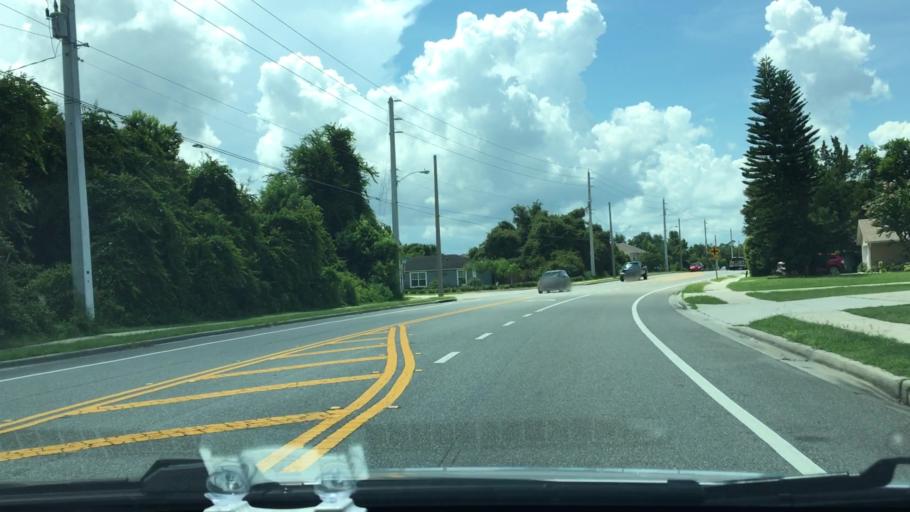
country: US
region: Florida
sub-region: Volusia County
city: Deltona
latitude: 28.8784
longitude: -81.2025
